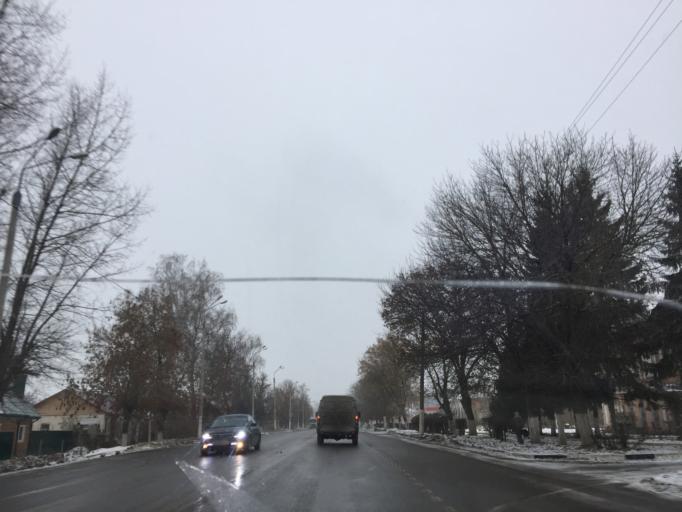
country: RU
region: Tula
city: Plavsk
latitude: 53.7039
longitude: 37.2890
